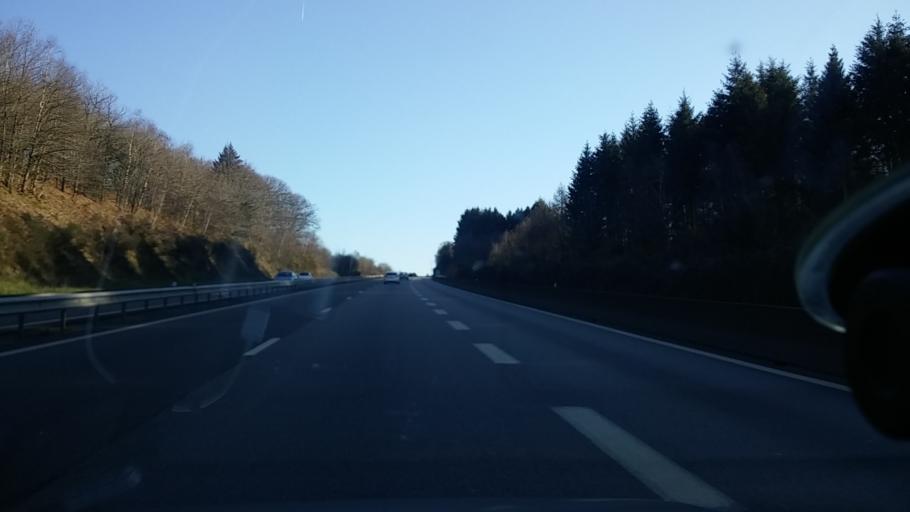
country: FR
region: Limousin
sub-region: Departement de la Haute-Vienne
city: Razes
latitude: 46.0661
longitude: 1.3610
